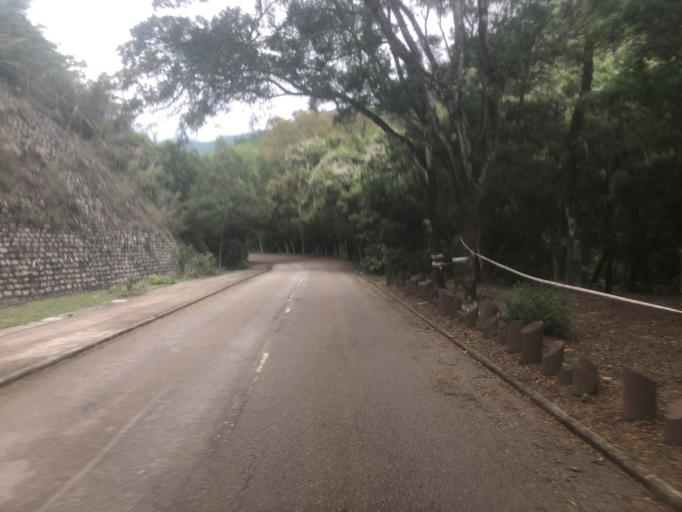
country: HK
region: Sai Kung
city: Sai Kung
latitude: 22.3985
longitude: 114.3257
